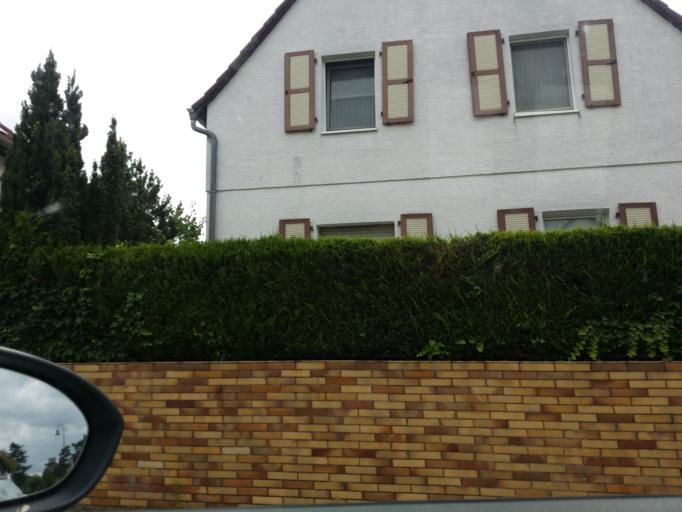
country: DE
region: Hesse
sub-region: Regierungsbezirk Darmstadt
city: Darmstadt
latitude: 49.8304
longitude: 8.6487
